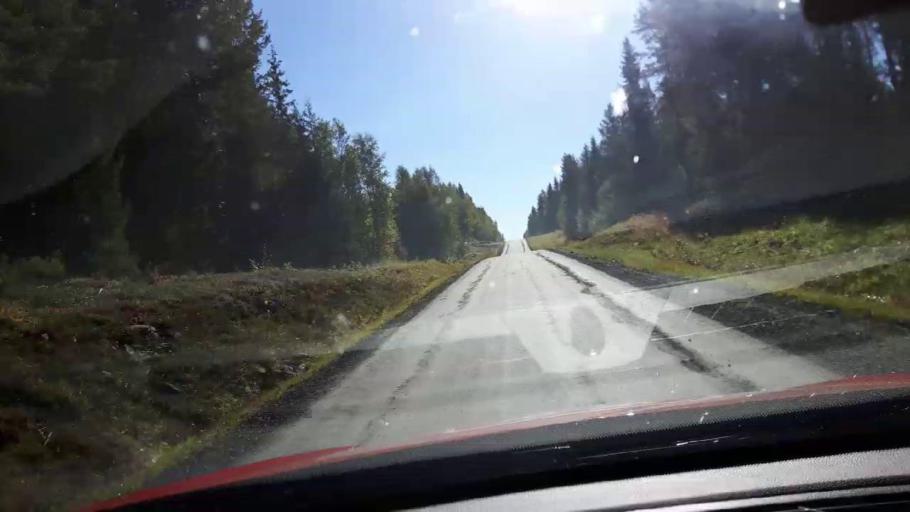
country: NO
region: Nord-Trondelag
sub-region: Lierne
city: Sandvika
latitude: 64.6076
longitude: 13.9602
